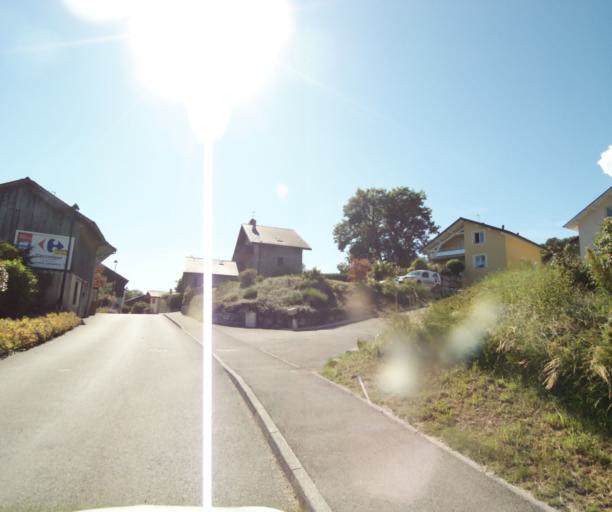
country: FR
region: Rhone-Alpes
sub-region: Departement de la Haute-Savoie
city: Ballaison
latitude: 46.2971
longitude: 6.3594
